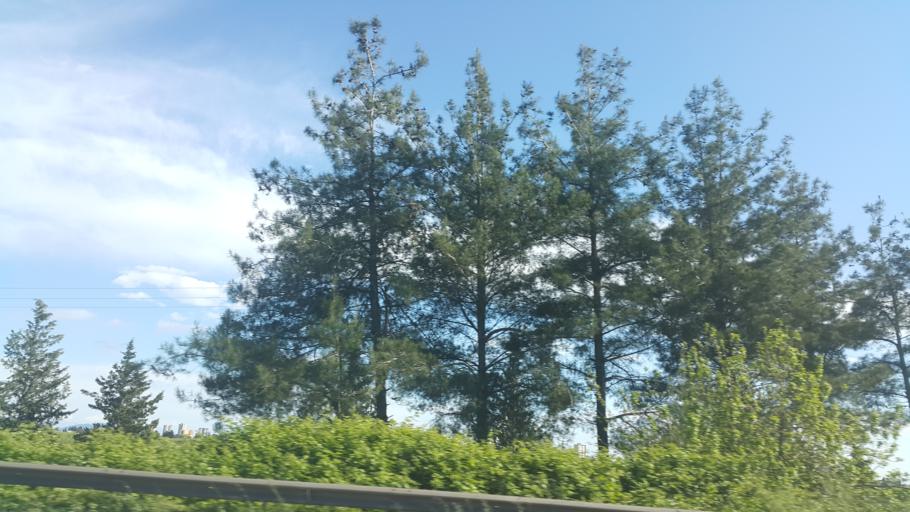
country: TR
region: Adana
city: Yuregir
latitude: 37.0286
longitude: 35.3829
